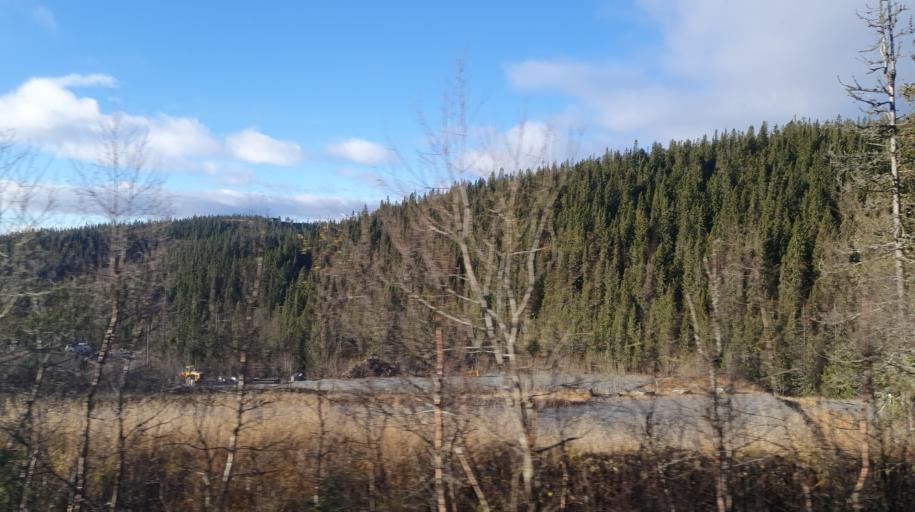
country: NO
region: Buskerud
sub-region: Krodsherad
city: Noresund
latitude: 60.2213
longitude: 9.5332
